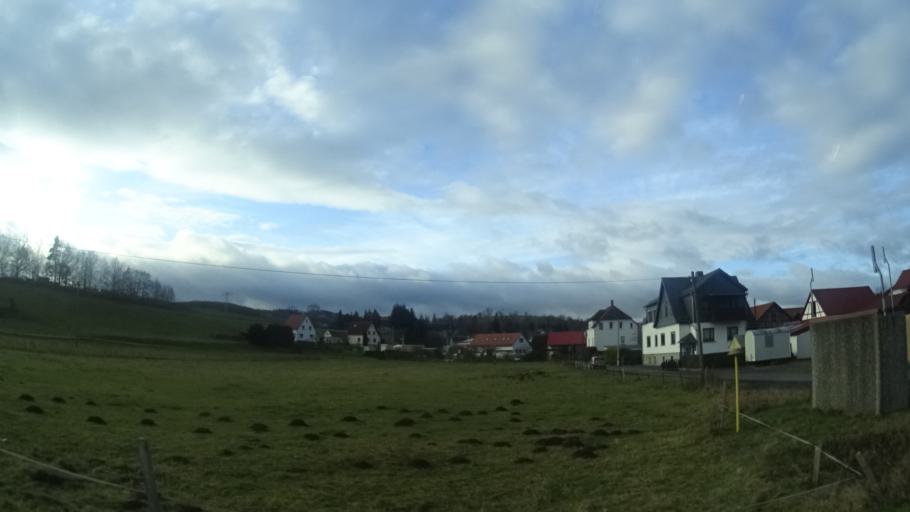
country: DE
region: Thuringia
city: Allendorf
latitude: 50.6704
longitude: 11.1471
